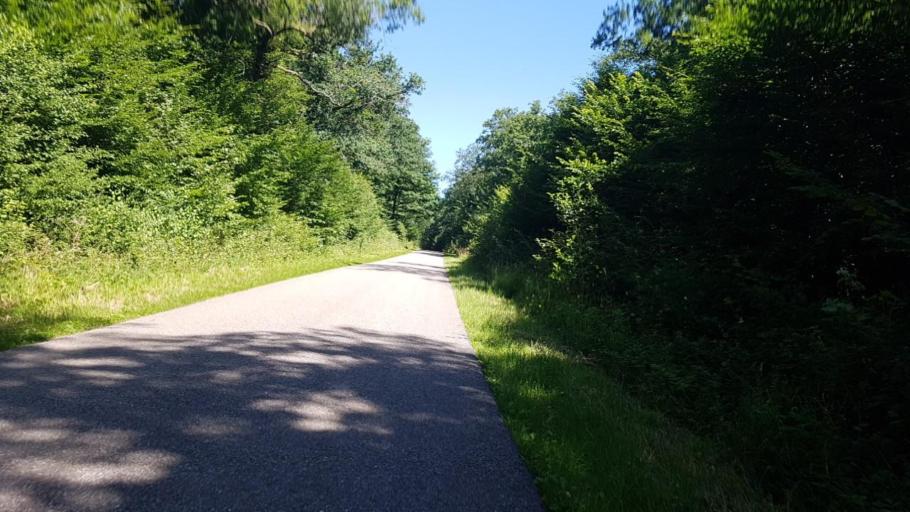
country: BE
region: Wallonia
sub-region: Province du Hainaut
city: Momignies
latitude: 50.0868
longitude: 4.2291
